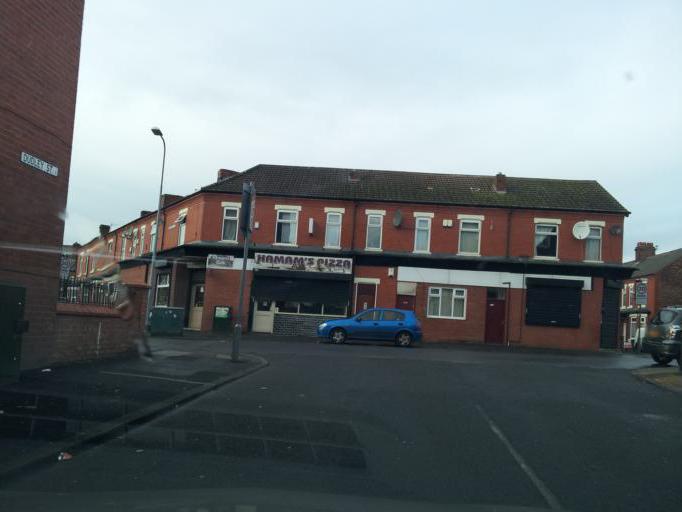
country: GB
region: England
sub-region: Manchester
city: Crumpsall
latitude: 53.5059
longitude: -2.2511
